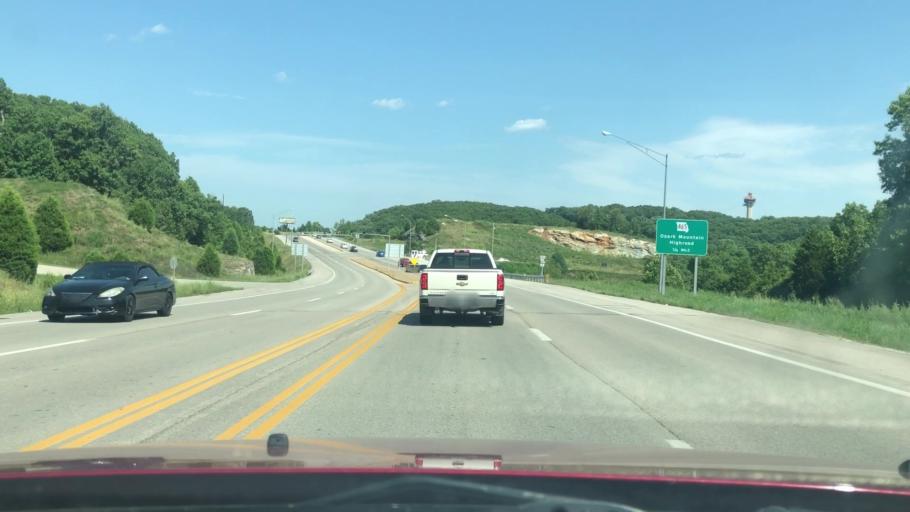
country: US
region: Missouri
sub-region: Stone County
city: Kimberling City
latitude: 36.6761
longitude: -93.3224
